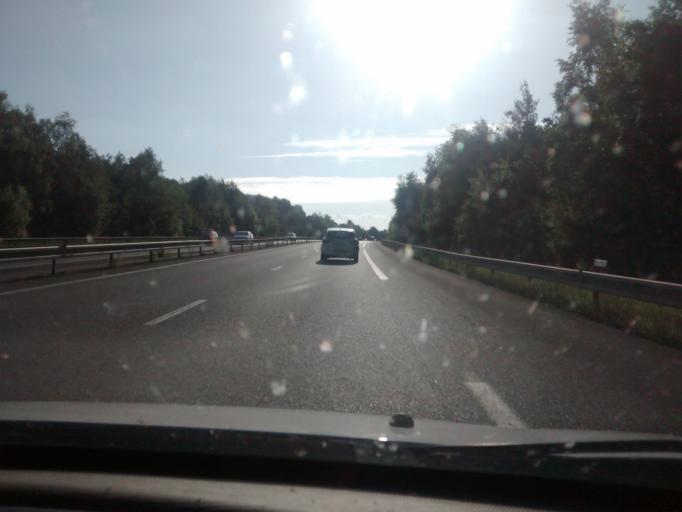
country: FR
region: Pays de la Loire
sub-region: Departement de la Mayenne
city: Port-Brillet
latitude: 48.0769
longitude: -0.9848
